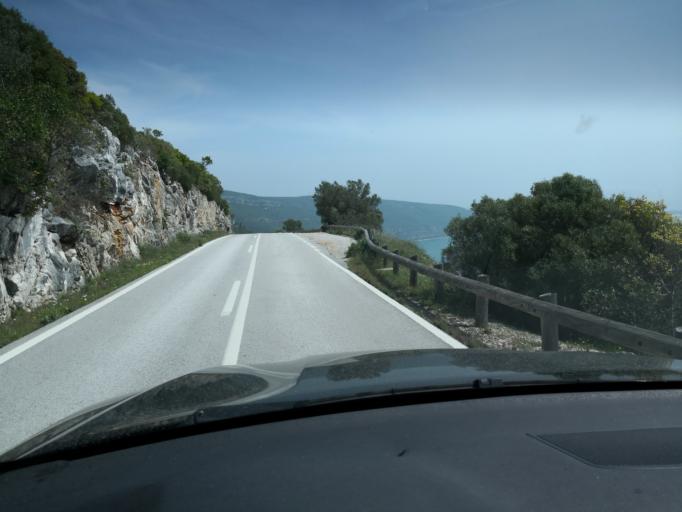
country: PT
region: Setubal
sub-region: Sesimbra
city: Sesimbra
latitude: 38.4675
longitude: -8.9998
